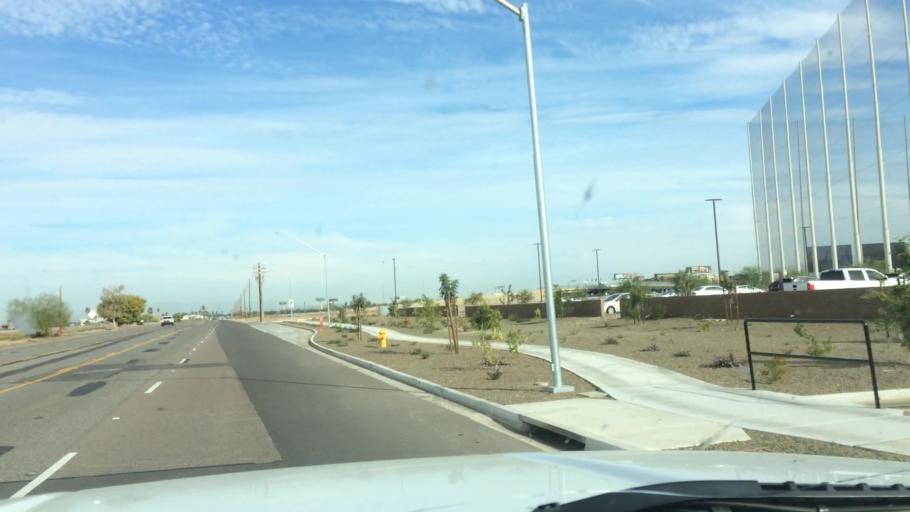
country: US
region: Arizona
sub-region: Maricopa County
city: Peoria
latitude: 33.5243
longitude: -112.2723
